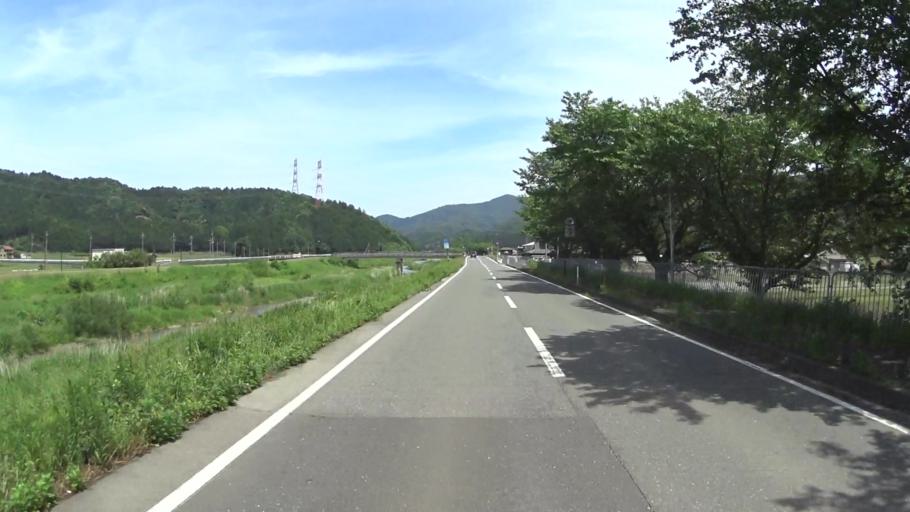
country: JP
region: Fukui
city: Obama
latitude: 35.4577
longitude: 135.5943
